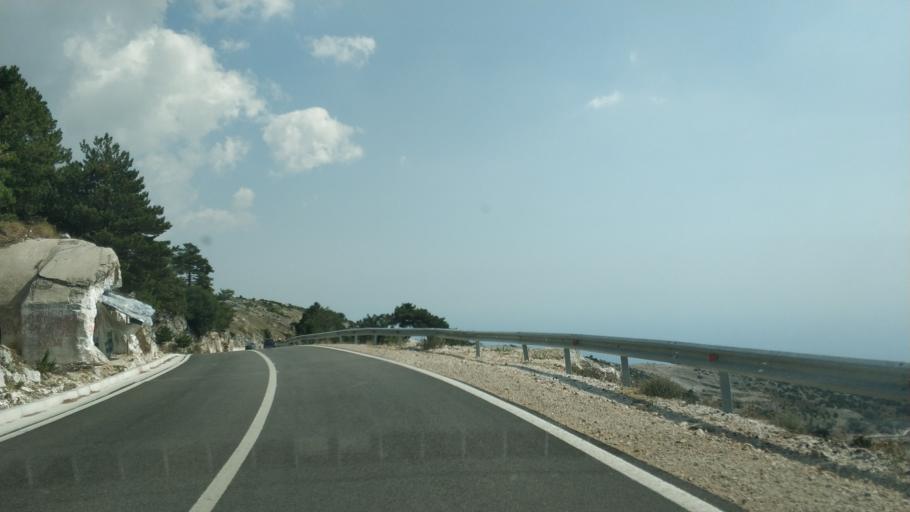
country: AL
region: Vlore
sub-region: Rrethi i Vlores
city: Vranisht
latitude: 40.1956
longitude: 19.5987
